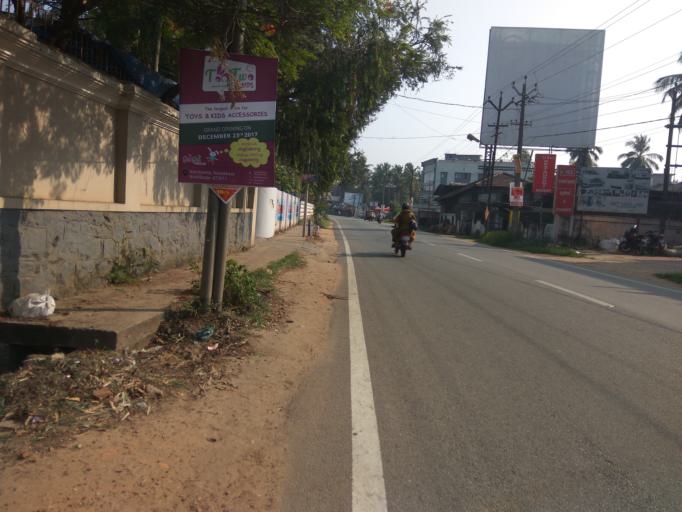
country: IN
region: Kerala
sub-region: Kozhikode
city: Kozhikode
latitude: 11.2910
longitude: 75.7649
